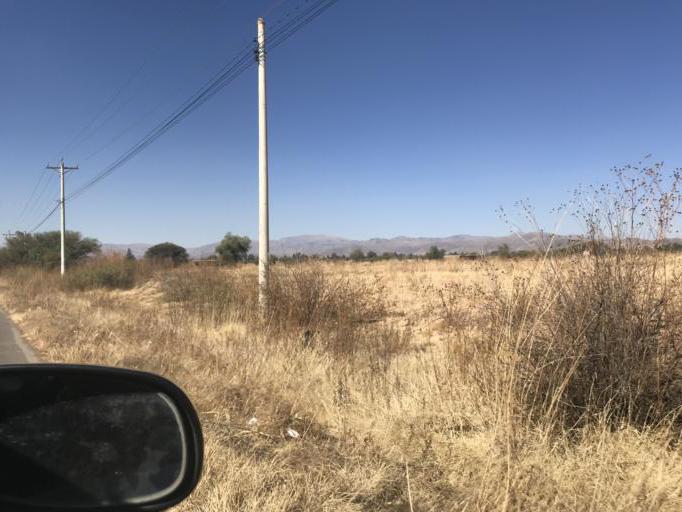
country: BO
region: Cochabamba
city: Cliza
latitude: -17.6000
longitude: -65.9666
